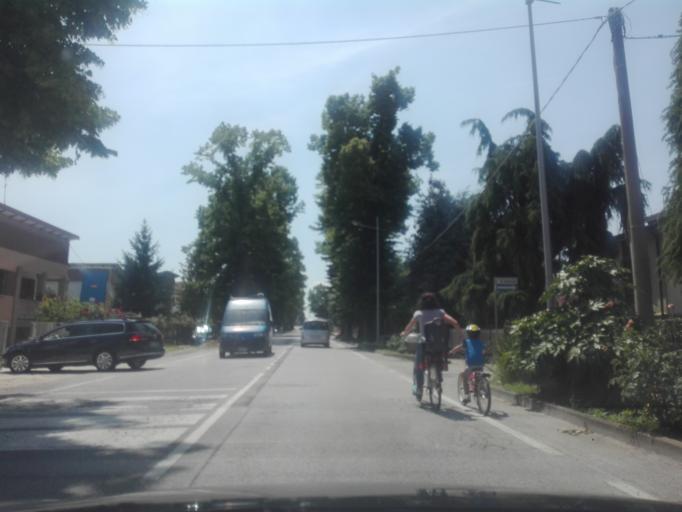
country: IT
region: Veneto
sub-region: Provincia di Rovigo
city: Adria
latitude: 45.0564
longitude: 12.0479
